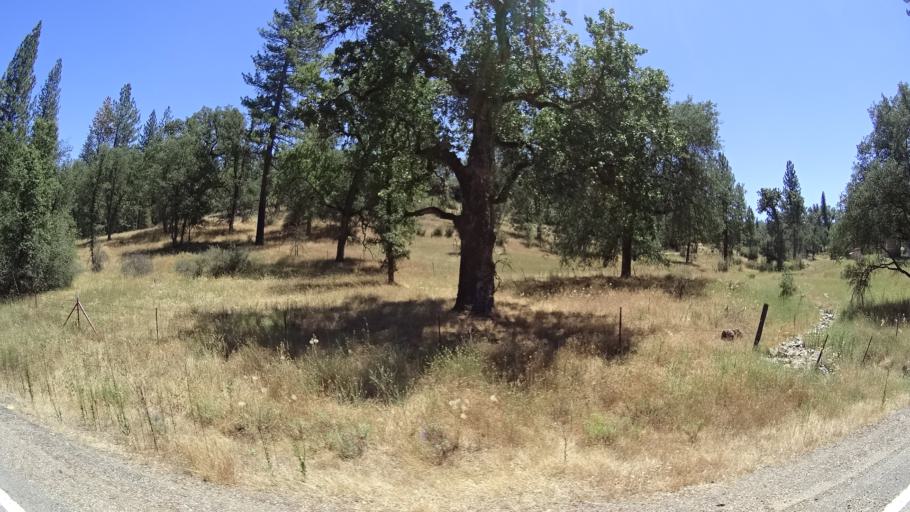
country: US
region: California
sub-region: Calaveras County
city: Mountain Ranch
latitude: 38.2660
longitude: -120.5043
